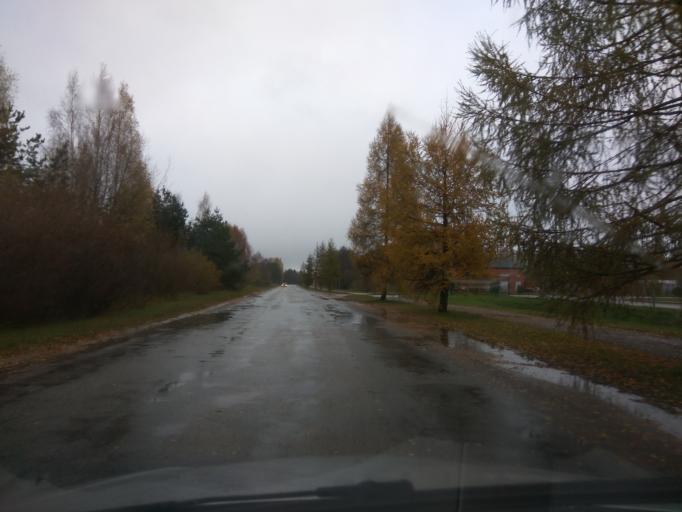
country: LV
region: Kuldigas Rajons
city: Kuldiga
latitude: 56.9725
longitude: 21.9477
